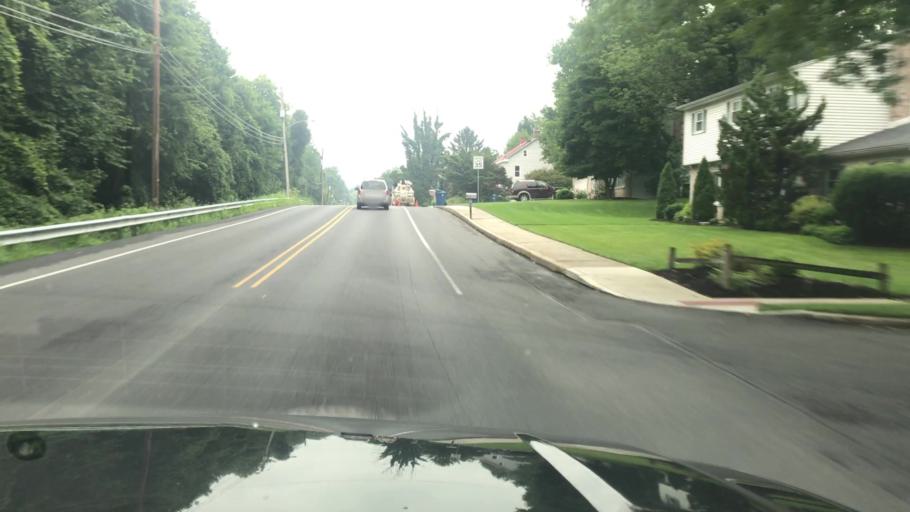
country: US
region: Pennsylvania
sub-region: Cumberland County
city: Shiremanstown
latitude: 40.2521
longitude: -76.9579
